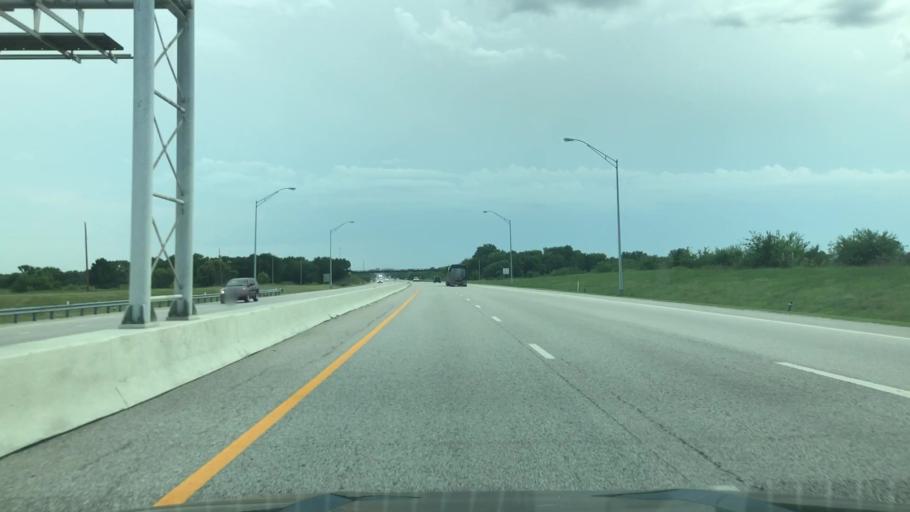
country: US
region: Oklahoma
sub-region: Craig County
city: Vinita
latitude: 36.6013
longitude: -95.1900
